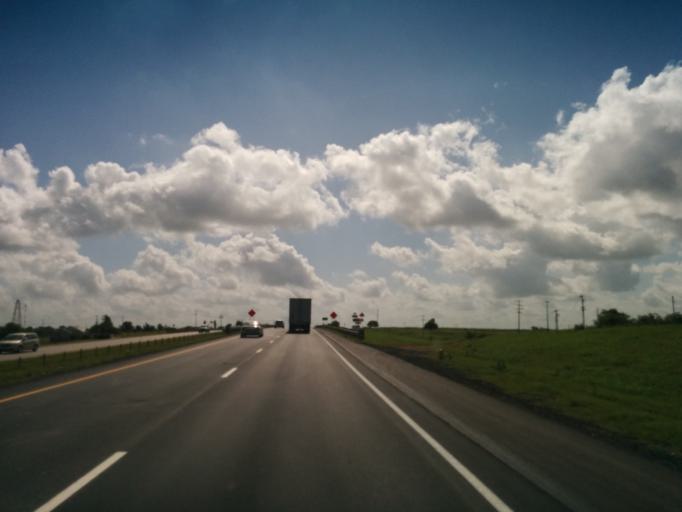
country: US
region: Texas
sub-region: Colorado County
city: Weimar
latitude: 29.6909
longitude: -96.7863
